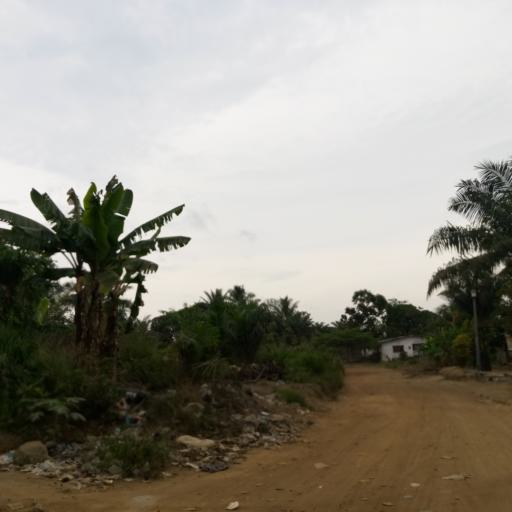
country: LR
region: Montserrado
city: Monrovia
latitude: 6.2926
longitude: -10.6795
